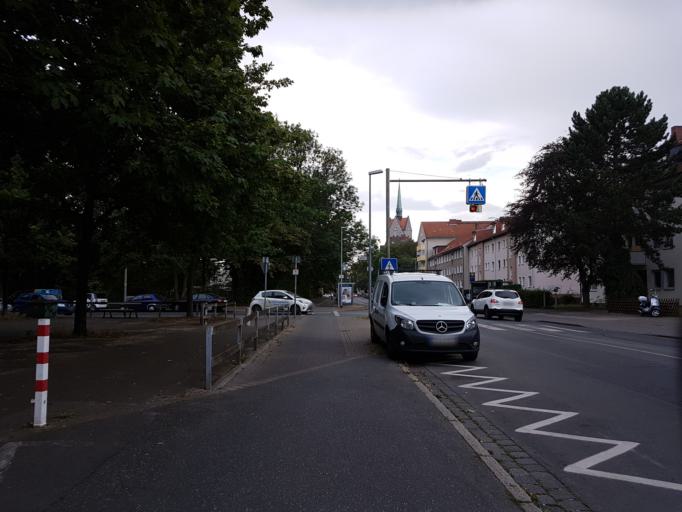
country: DE
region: Lower Saxony
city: Hannover
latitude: 52.3972
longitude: 9.7491
